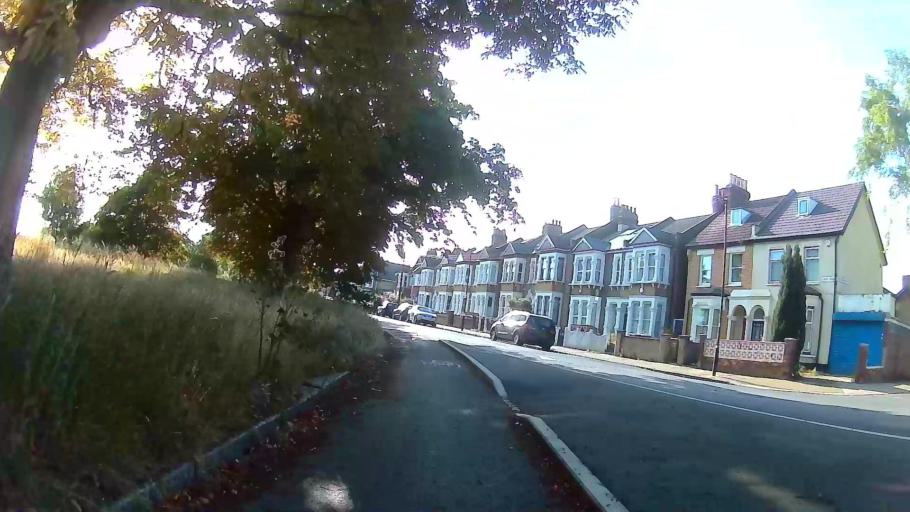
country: GB
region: England
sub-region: Greater London
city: East Ham
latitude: 51.5544
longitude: 0.0293
